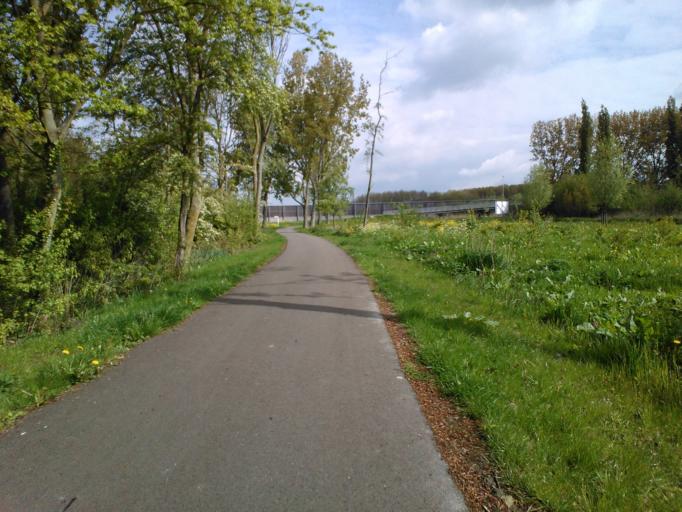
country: NL
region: South Holland
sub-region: Gemeente Vlaardingen
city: Vlaardingen
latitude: 51.9172
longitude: 4.3103
